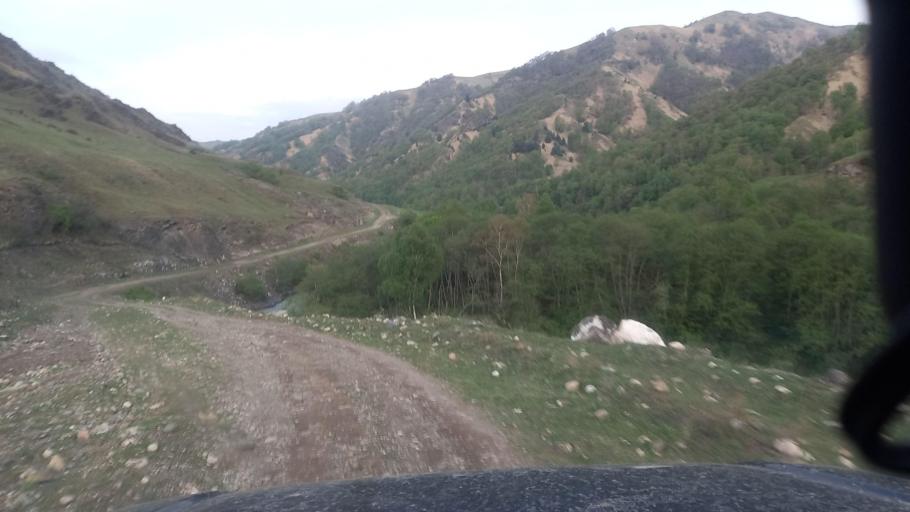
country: RU
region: Kabardino-Balkariya
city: Kamennomostskoye
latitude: 43.7196
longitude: 42.8741
